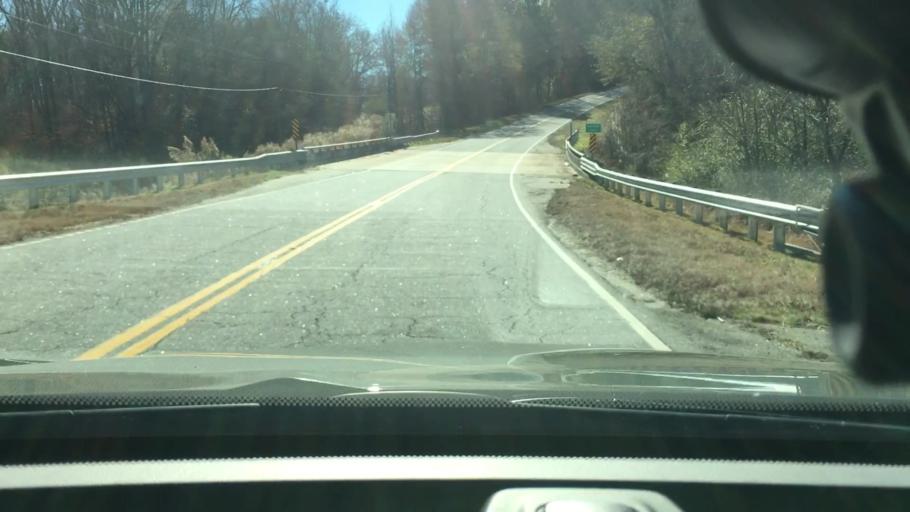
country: US
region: South Carolina
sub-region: Spartanburg County
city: Pacolet
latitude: 34.9659
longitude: -81.7056
